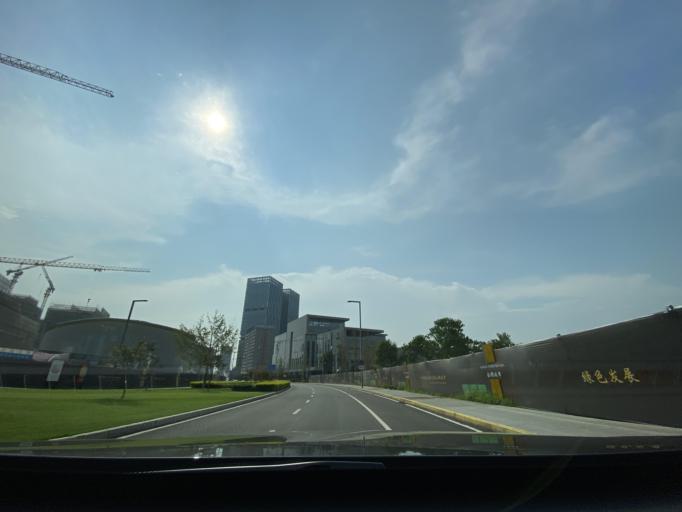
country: CN
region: Sichuan
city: Dongsheng
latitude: 30.3954
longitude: 104.0757
